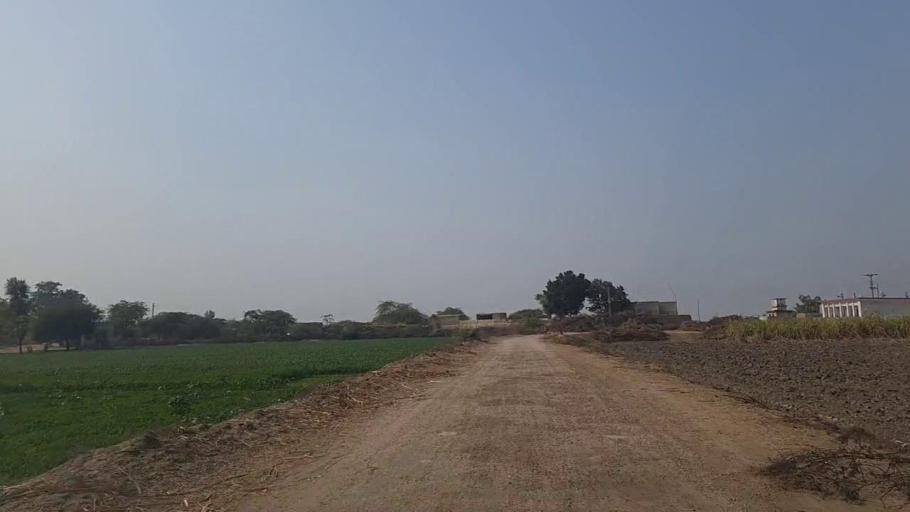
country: PK
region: Sindh
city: Daur
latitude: 26.4325
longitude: 68.4438
